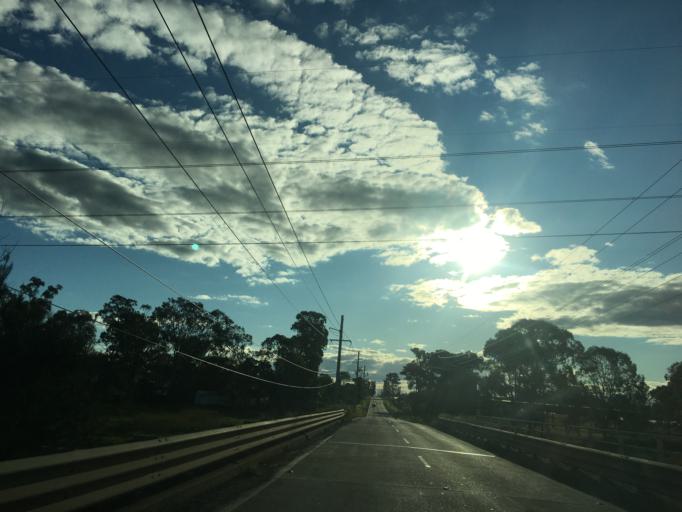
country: AU
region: New South Wales
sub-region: Fairfield
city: Cecil Park
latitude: -33.9162
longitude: 150.7959
